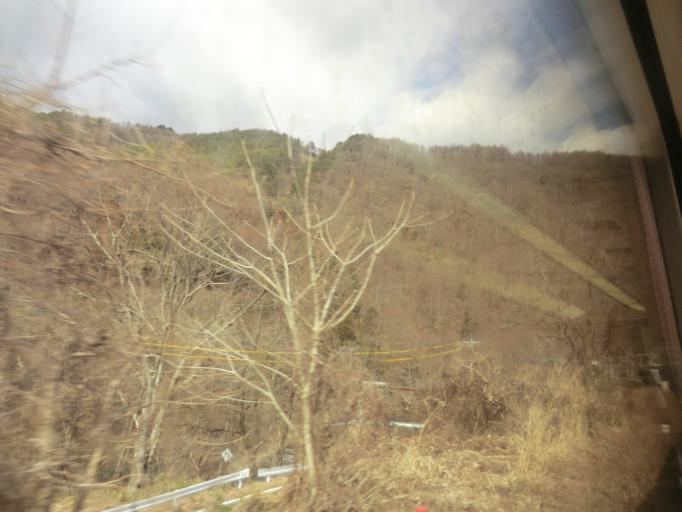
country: JP
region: Nagano
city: Ina
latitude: 35.8976
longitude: 137.7675
